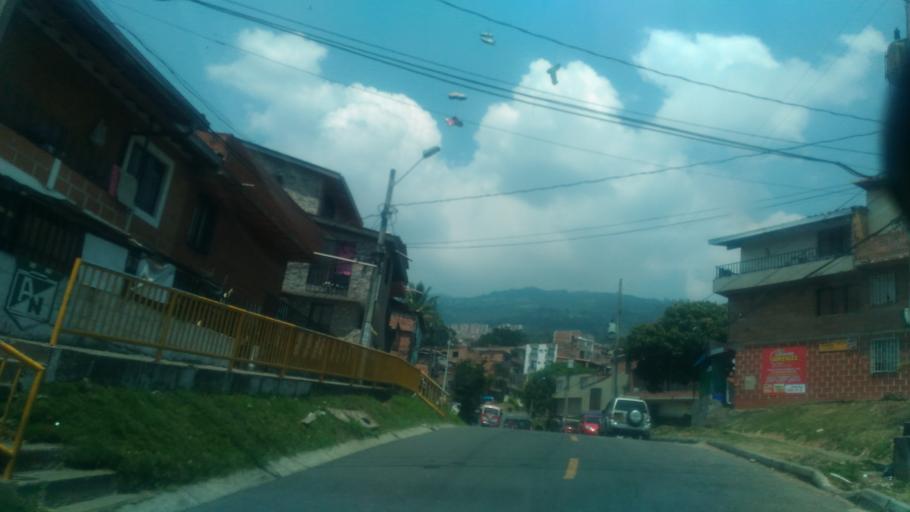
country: CO
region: Antioquia
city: Medellin
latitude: 6.2800
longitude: -75.5907
